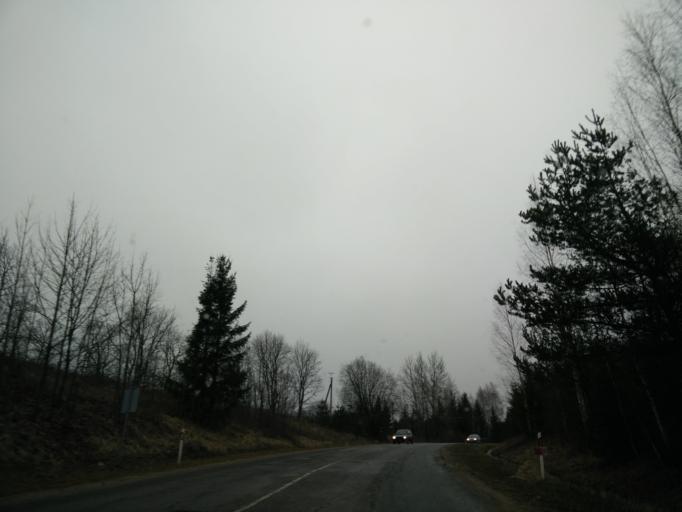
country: LT
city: Ariogala
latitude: 55.3047
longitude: 23.4330
